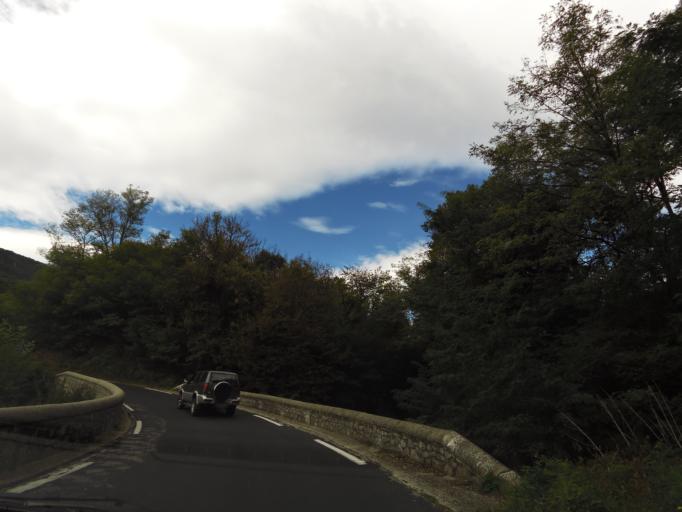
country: FR
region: Languedoc-Roussillon
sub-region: Departement du Gard
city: Lasalle
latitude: 44.0129
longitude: 3.8517
